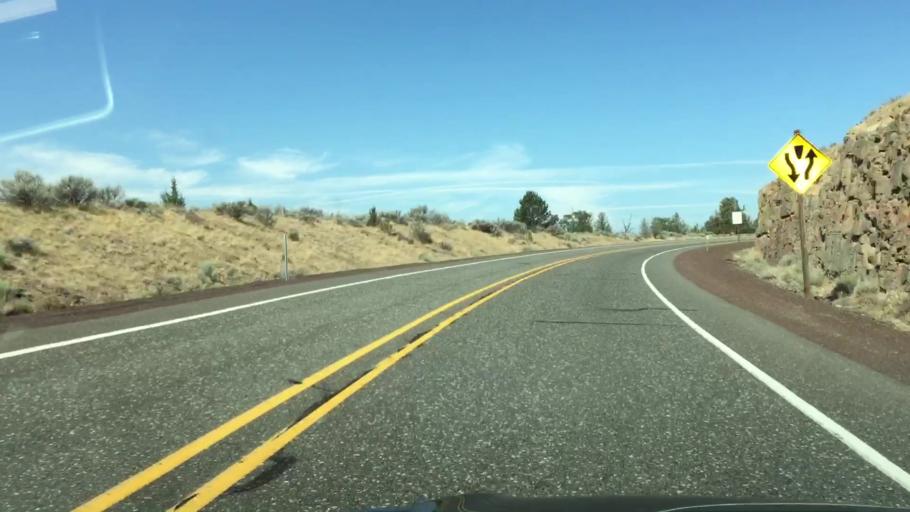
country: US
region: Oregon
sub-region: Jefferson County
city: Warm Springs
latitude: 45.1676
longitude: -121.1169
